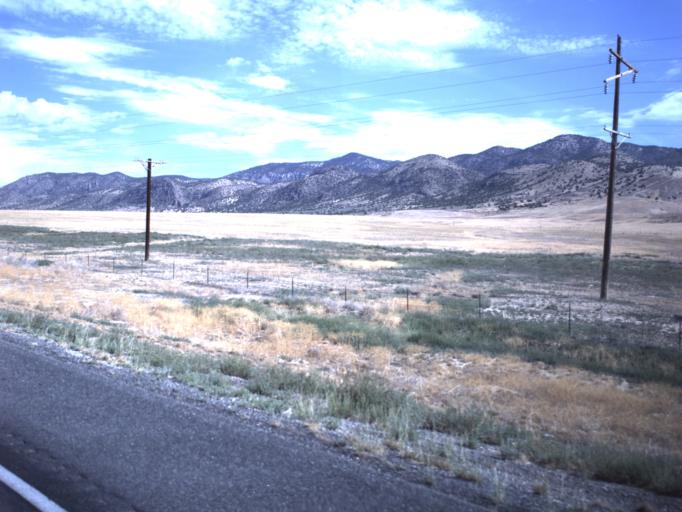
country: US
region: Utah
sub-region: Sanpete County
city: Gunnison
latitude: 39.2379
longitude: -111.8490
